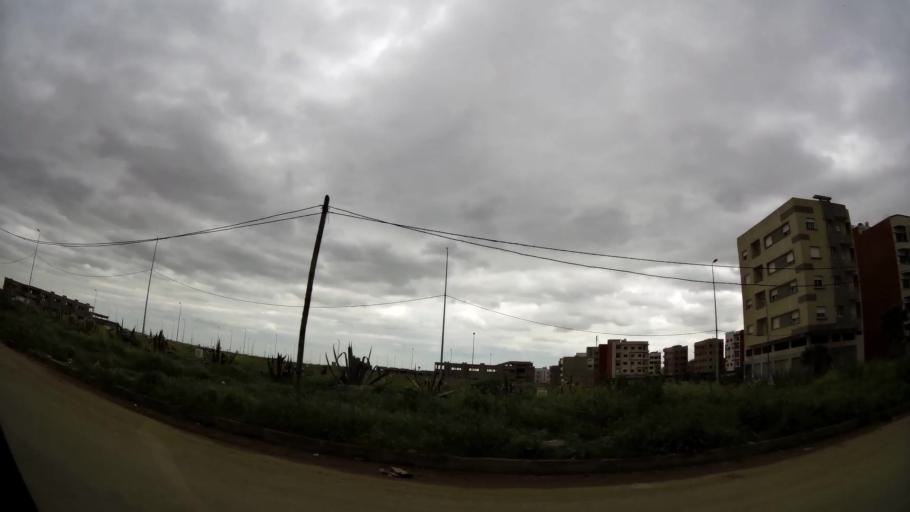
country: MA
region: Grand Casablanca
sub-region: Mediouna
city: Tit Mellil
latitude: 33.5550
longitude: -7.5337
